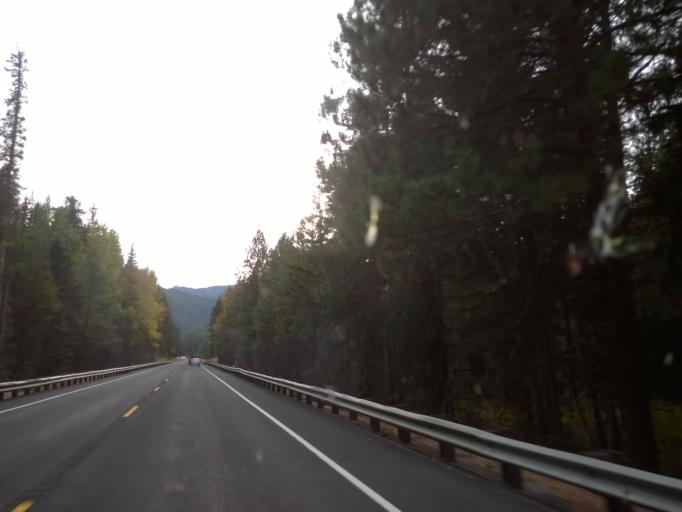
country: US
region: Washington
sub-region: Chelan County
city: Leavenworth
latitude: 47.3277
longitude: -120.6645
